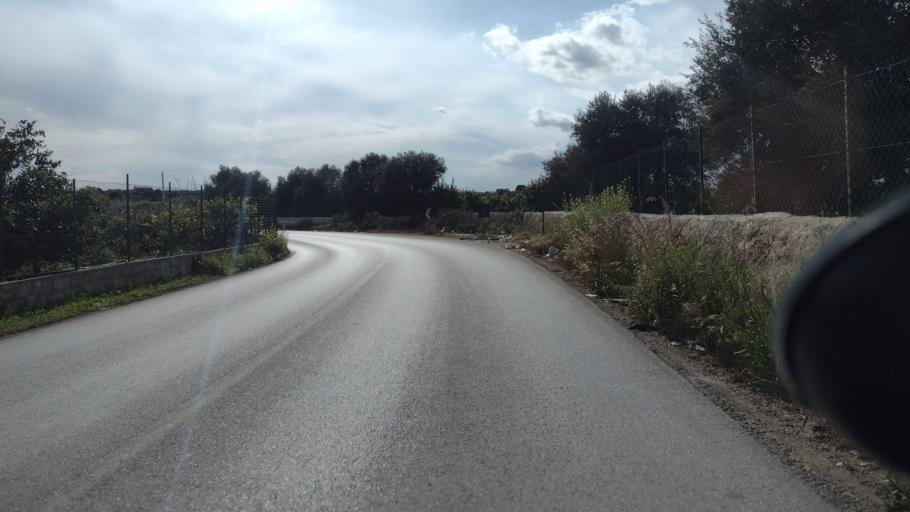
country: IT
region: Sicily
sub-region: Provincia di Siracusa
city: Avola
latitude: 36.8790
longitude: 15.1288
